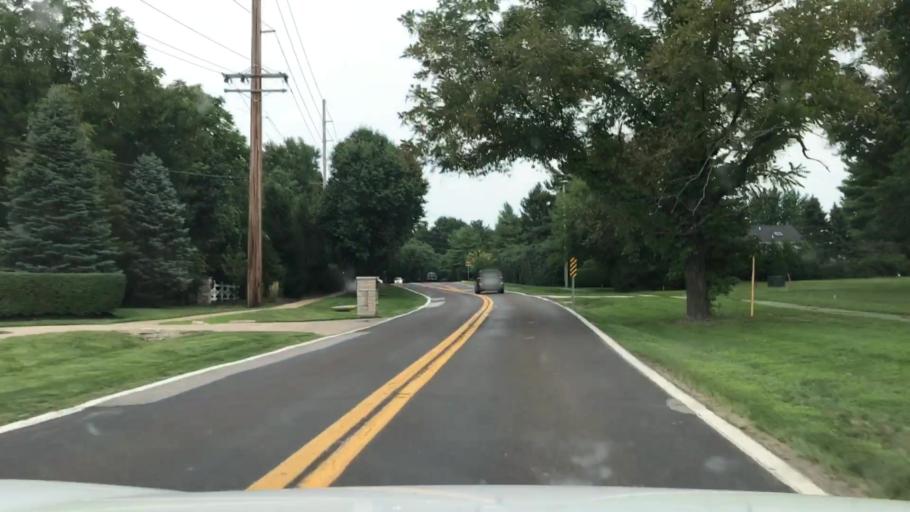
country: US
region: Missouri
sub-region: Saint Louis County
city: Clarkson Valley
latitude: 38.6275
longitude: -90.5950
